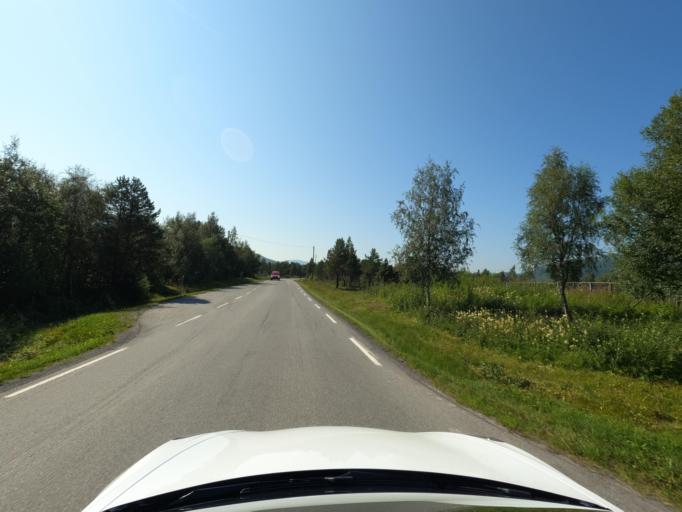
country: NO
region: Nordland
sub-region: Ballangen
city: Ballangen
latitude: 68.3569
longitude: 16.8704
